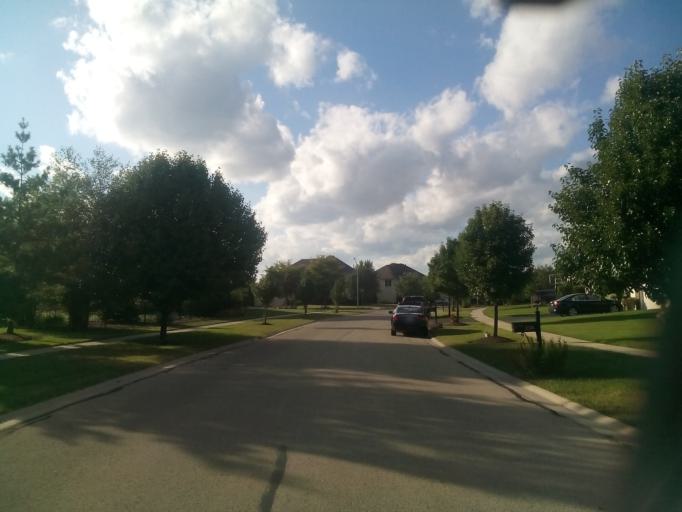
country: US
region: Illinois
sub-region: Will County
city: Romeoville
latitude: 41.6875
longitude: -88.1536
